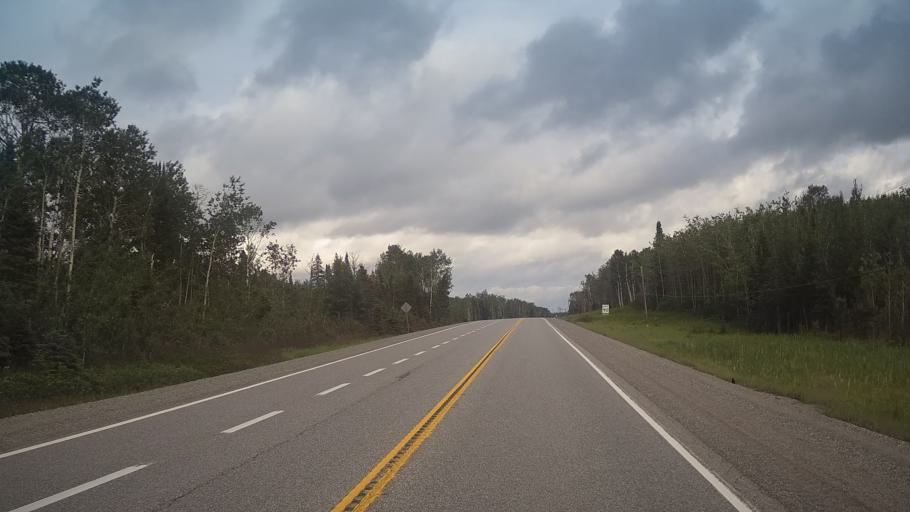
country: CA
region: Ontario
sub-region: Rainy River District
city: Atikokan
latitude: 49.0086
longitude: -90.4190
